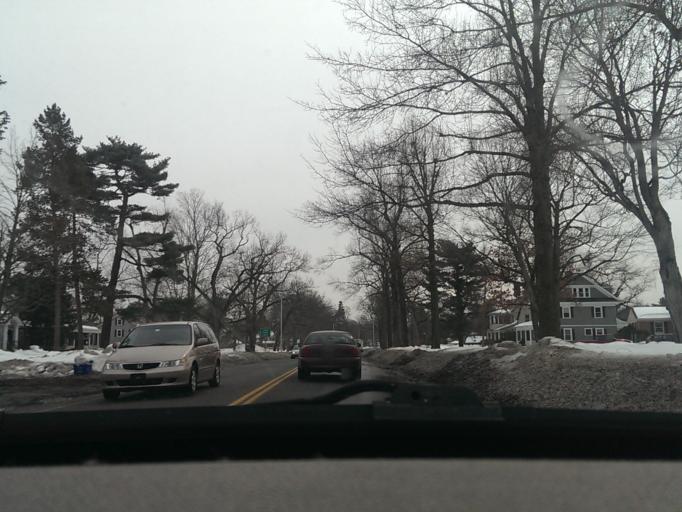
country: US
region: Massachusetts
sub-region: Hampden County
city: Longmeadow
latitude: 42.0690
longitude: -72.5799
